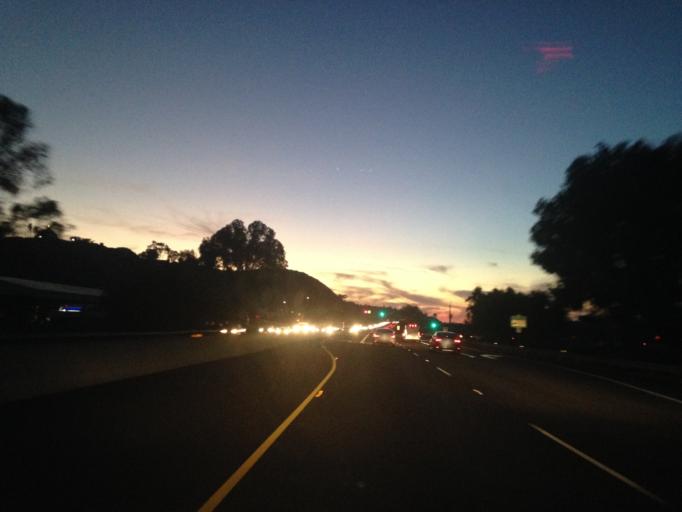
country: US
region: California
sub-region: San Diego County
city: Camp Pendleton South
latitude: 33.2155
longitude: -117.3550
